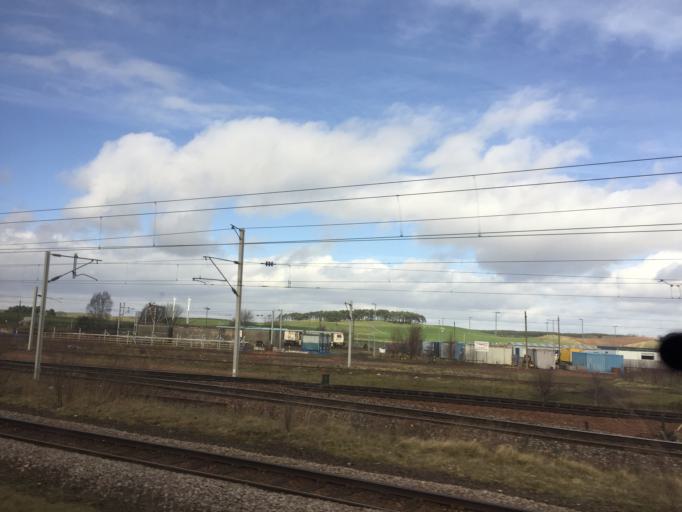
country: GB
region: Scotland
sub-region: South Lanarkshire
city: Carnwath
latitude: 55.6899
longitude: -3.6651
